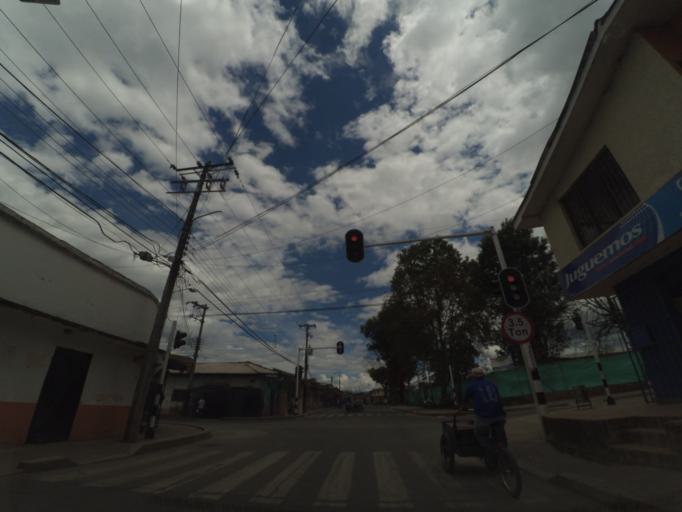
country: CO
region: Cauca
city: Popayan
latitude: 2.4336
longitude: -76.6049
